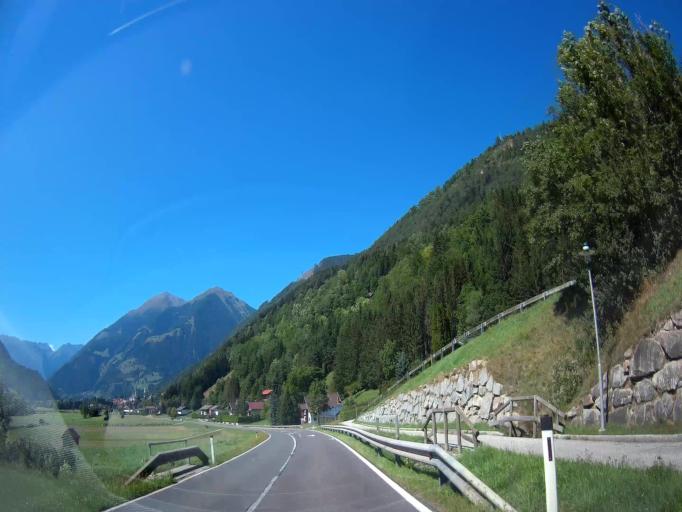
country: AT
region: Carinthia
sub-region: Politischer Bezirk Spittal an der Drau
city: Obervellach
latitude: 46.9261
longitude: 13.2214
